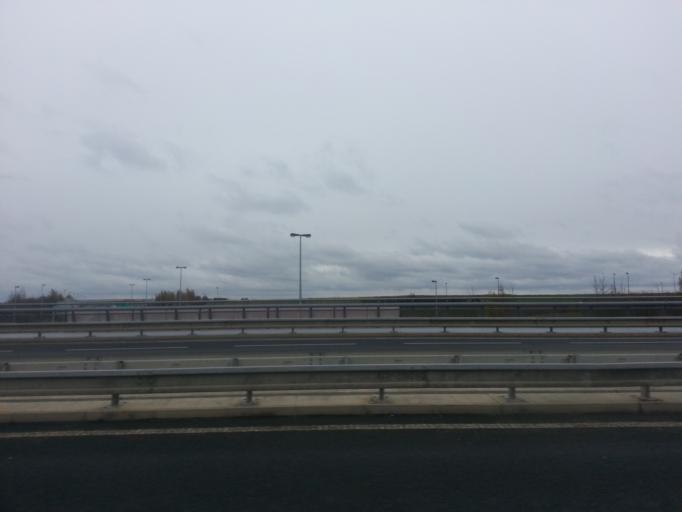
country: CZ
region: Central Bohemia
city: Hostivice
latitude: 50.0939
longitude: 14.2964
